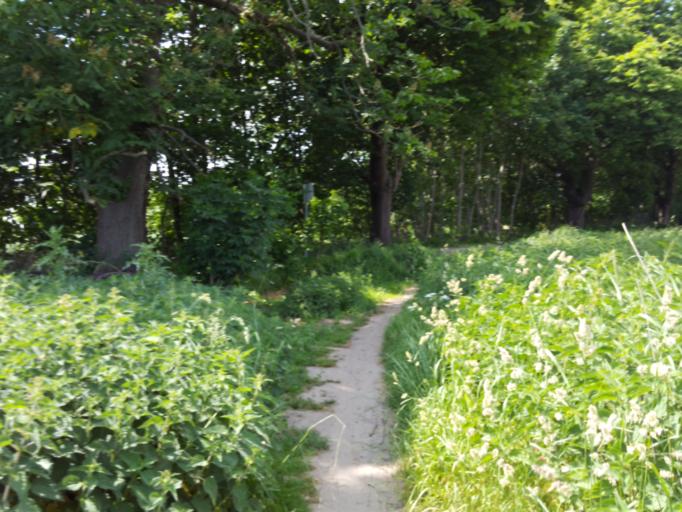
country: DE
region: Mecklenburg-Vorpommern
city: Kramerhof
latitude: 54.3353
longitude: 13.0399
